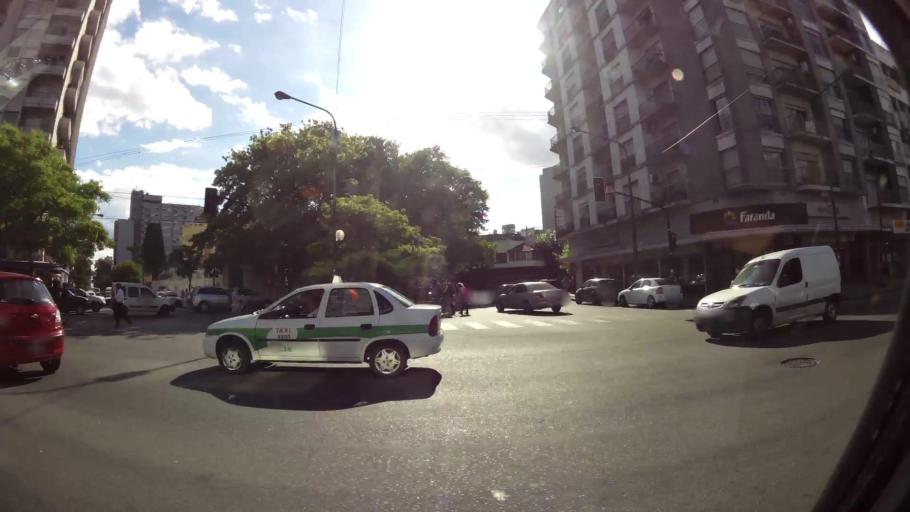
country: AR
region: Buenos Aires
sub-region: Partido de La Plata
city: La Plata
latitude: -34.9101
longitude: -57.9488
